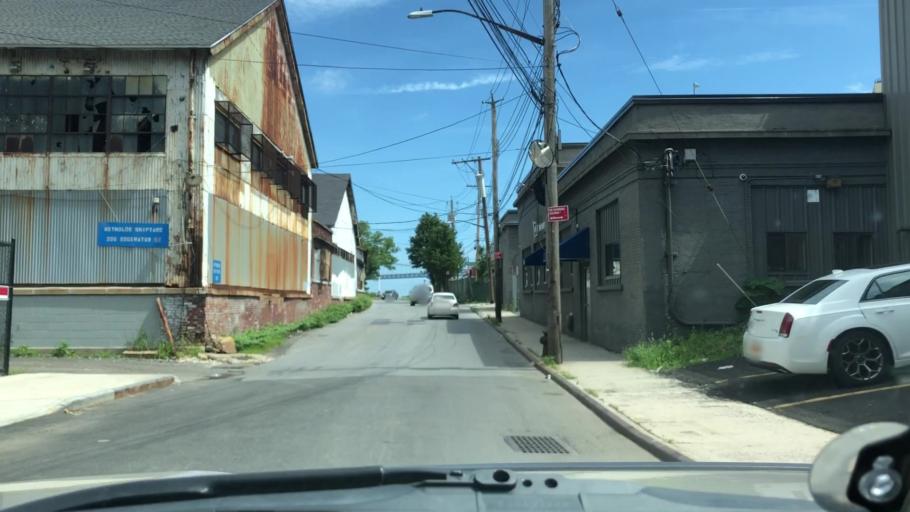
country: US
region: New Jersey
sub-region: Hudson County
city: Bayonne
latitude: 40.6171
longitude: -74.0657
